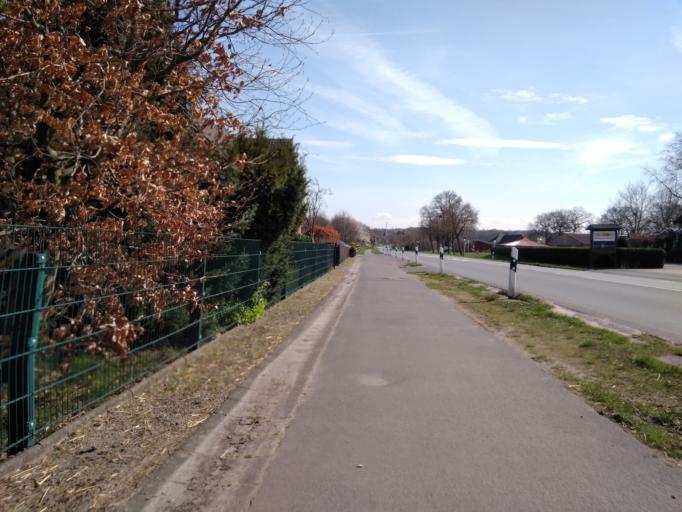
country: DE
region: North Rhine-Westphalia
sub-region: Regierungsbezirk Dusseldorf
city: Schermbeck
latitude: 51.6582
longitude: 6.9015
